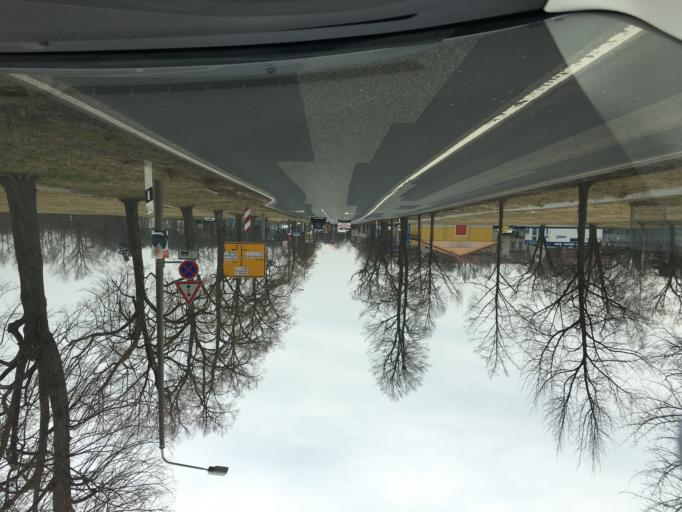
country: DE
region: Thuringia
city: Altenburg
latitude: 51.0049
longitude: 12.4516
